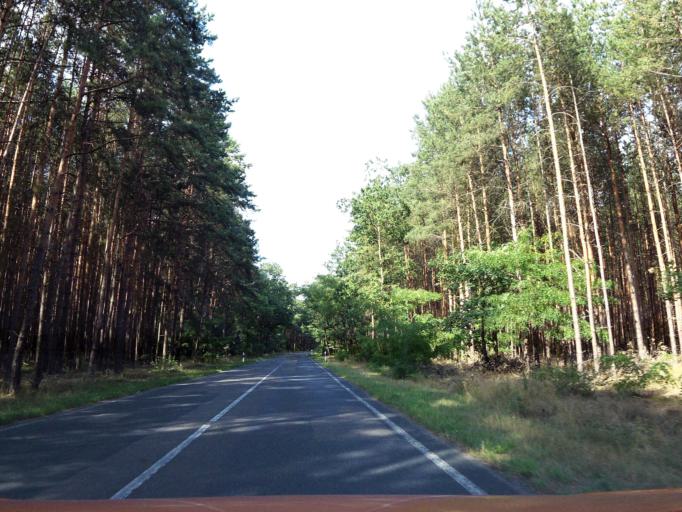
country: DE
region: Brandenburg
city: Michendorf
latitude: 52.2885
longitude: 13.1136
